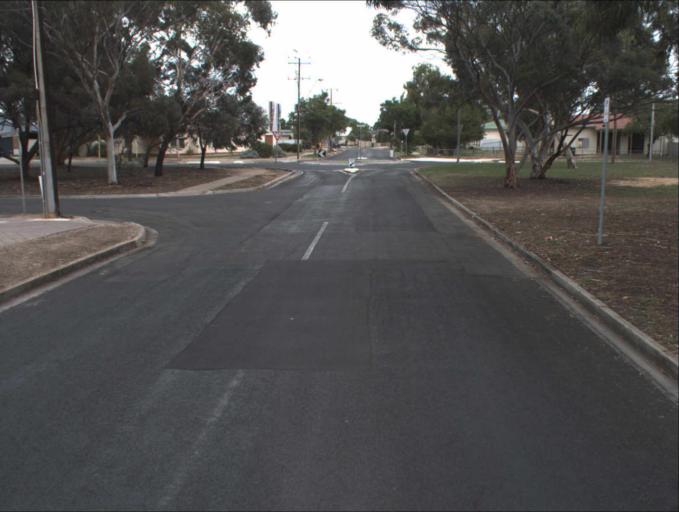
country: AU
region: South Australia
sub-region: Port Adelaide Enfield
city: Enfield
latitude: -34.8551
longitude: 138.6238
